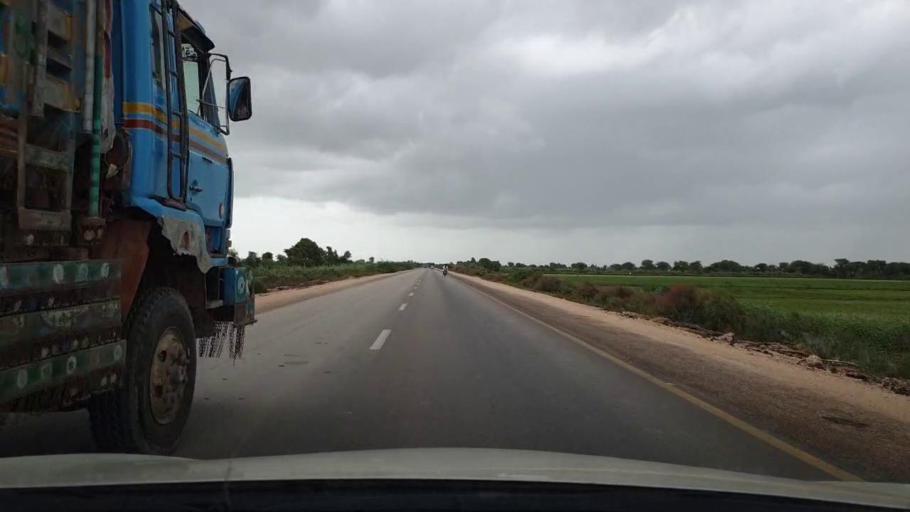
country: PK
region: Sindh
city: Mirpur Batoro
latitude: 24.6429
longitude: 68.4529
